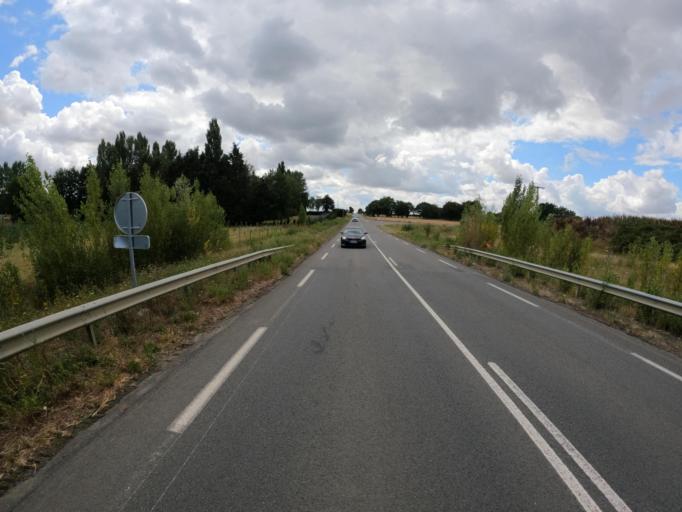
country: FR
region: Pays de la Loire
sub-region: Departement de la Sarthe
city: Solesmes
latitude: 47.8688
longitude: -0.3107
